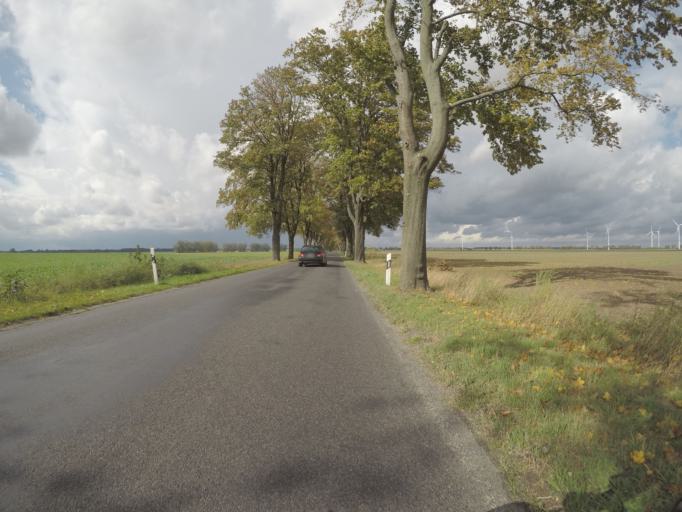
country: DE
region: Brandenburg
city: Altlandsberg
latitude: 52.5903
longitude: 13.7775
